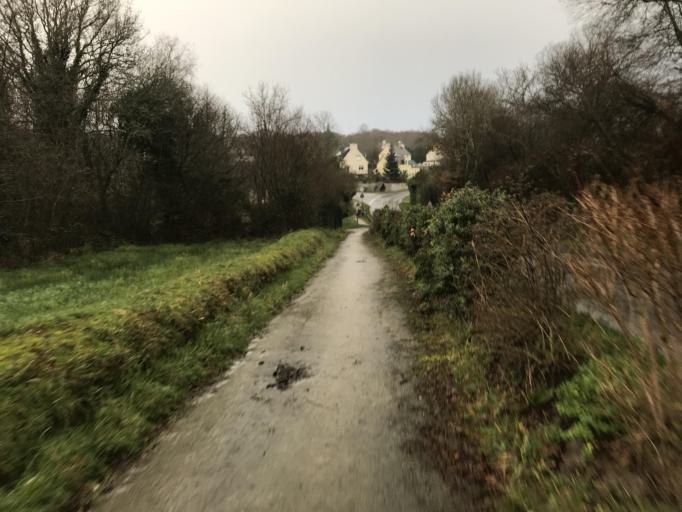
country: FR
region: Brittany
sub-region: Departement du Finistere
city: Loperhet
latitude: 48.3647
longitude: -4.3095
